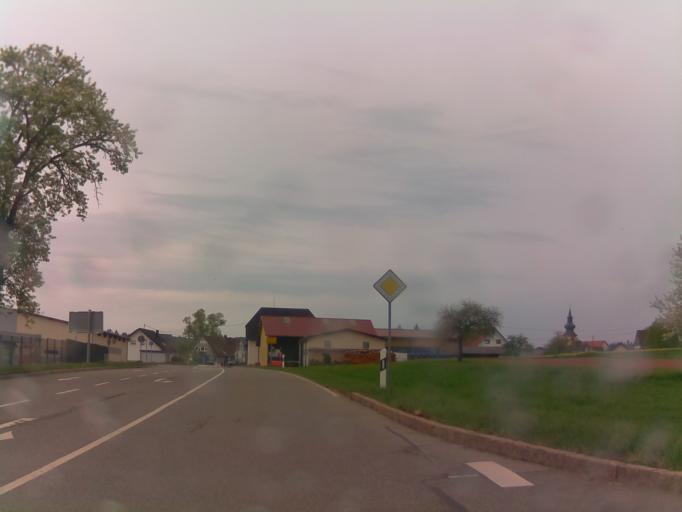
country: DE
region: Baden-Wuerttemberg
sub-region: Freiburg Region
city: Monchweiler
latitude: 48.1090
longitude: 8.4788
